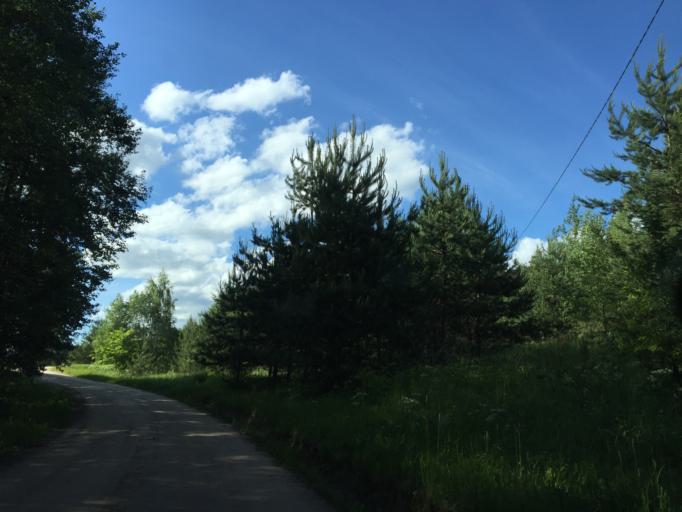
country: LV
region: Vecumnieki
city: Vecumnieki
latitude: 56.4444
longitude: 24.5796
